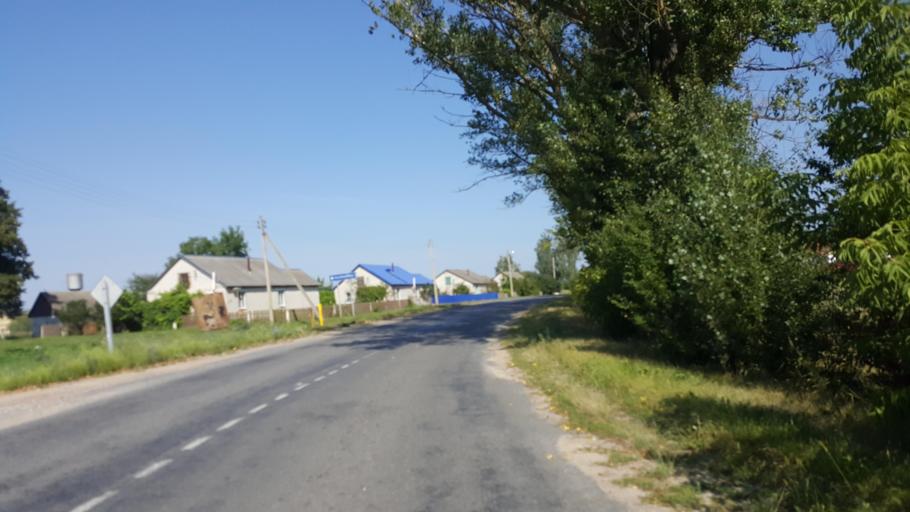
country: BY
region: Brest
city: Kamyanyets
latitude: 52.4316
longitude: 23.7497
